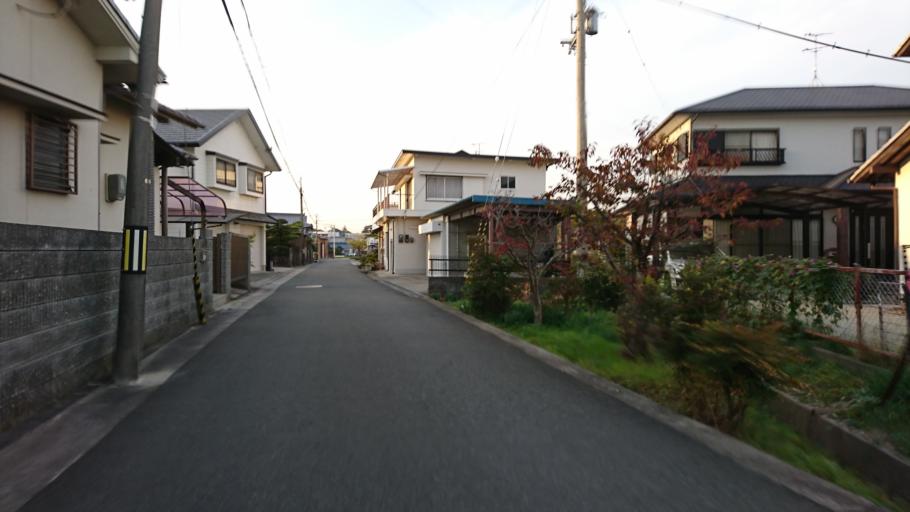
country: JP
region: Hyogo
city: Kakogawacho-honmachi
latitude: 34.7812
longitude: 134.8709
